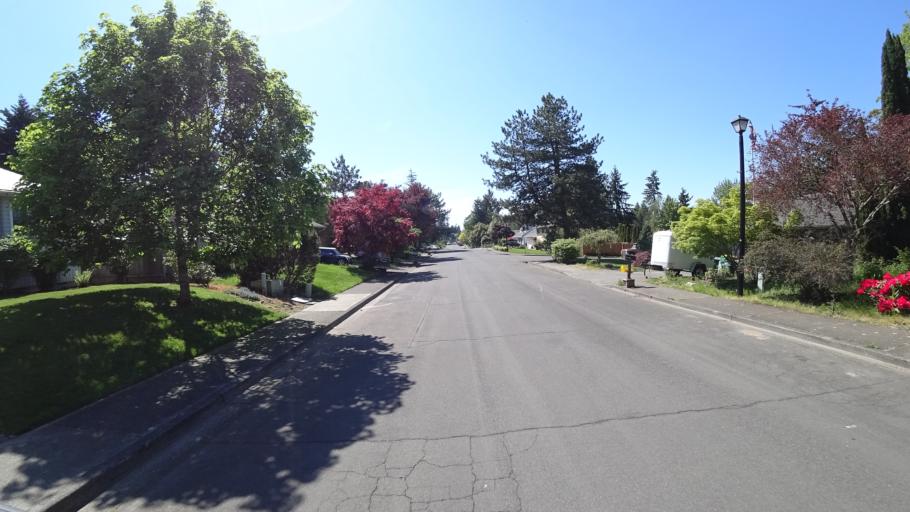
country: US
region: Oregon
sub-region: Washington County
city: Aloha
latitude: 45.4768
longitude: -122.8447
